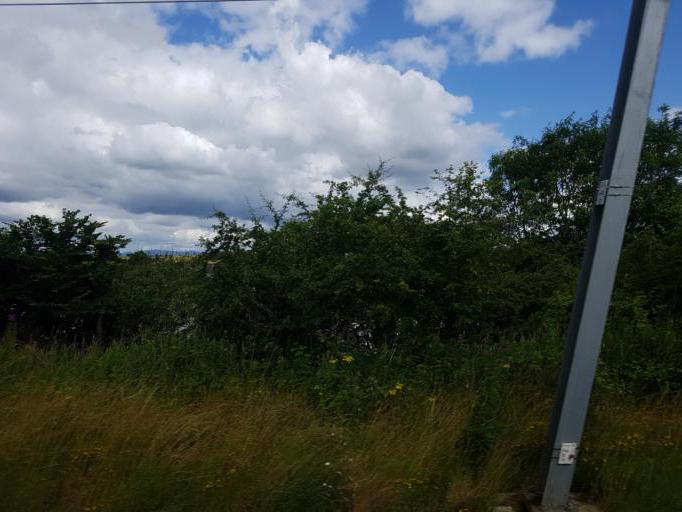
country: GB
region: Scotland
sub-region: West Lothian
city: Linlithgow
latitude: 55.9741
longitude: -3.6229
